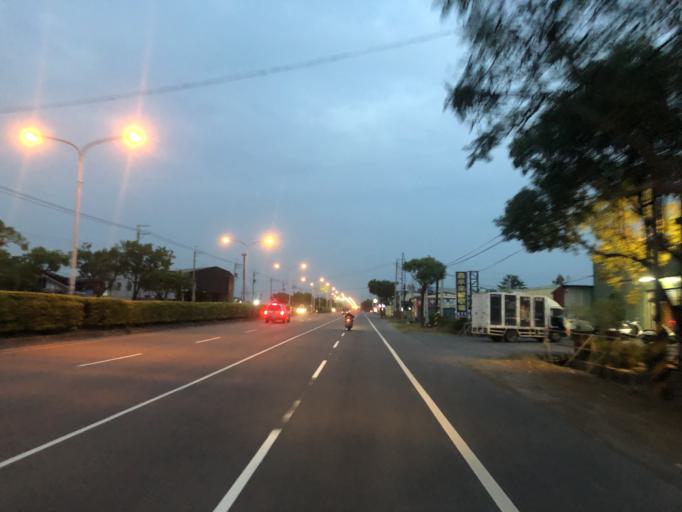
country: TW
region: Taiwan
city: Yujing
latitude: 23.1425
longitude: 120.3255
